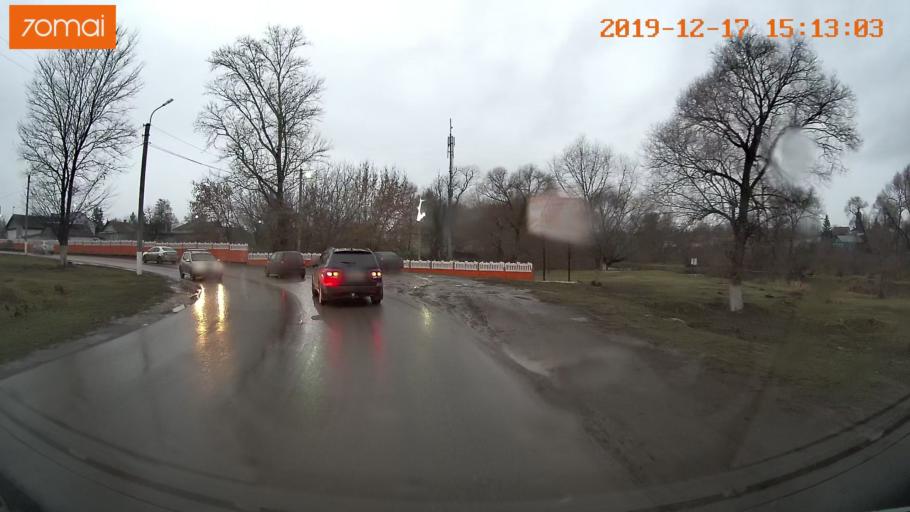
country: RU
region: Rjazan
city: Mikhaylov
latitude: 54.2347
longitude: 39.0216
